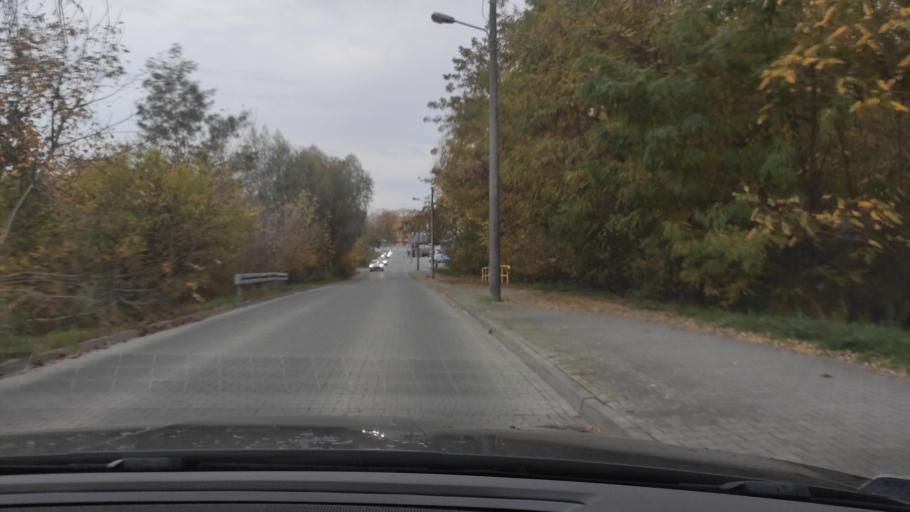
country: PL
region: Greater Poland Voivodeship
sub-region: Powiat poznanski
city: Swarzedz
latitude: 52.4074
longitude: 17.0612
